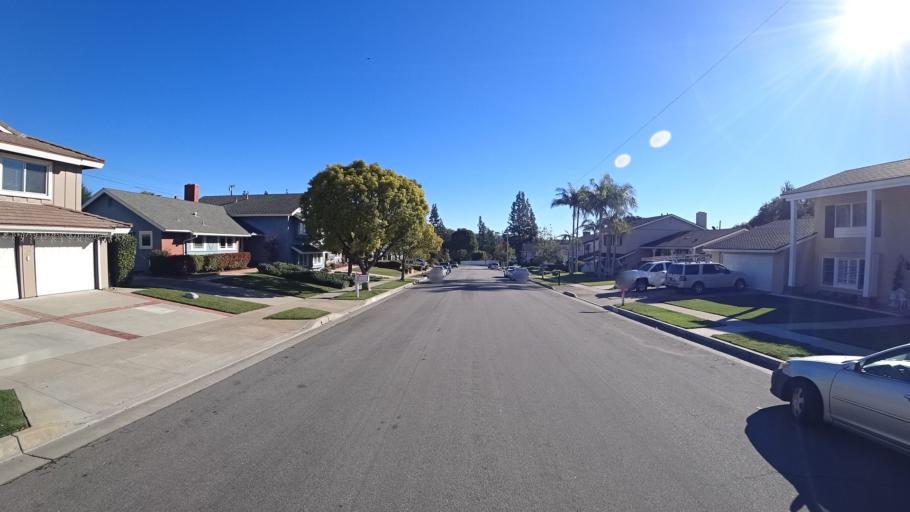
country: US
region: California
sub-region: Orange County
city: La Habra
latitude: 33.9432
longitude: -117.9264
